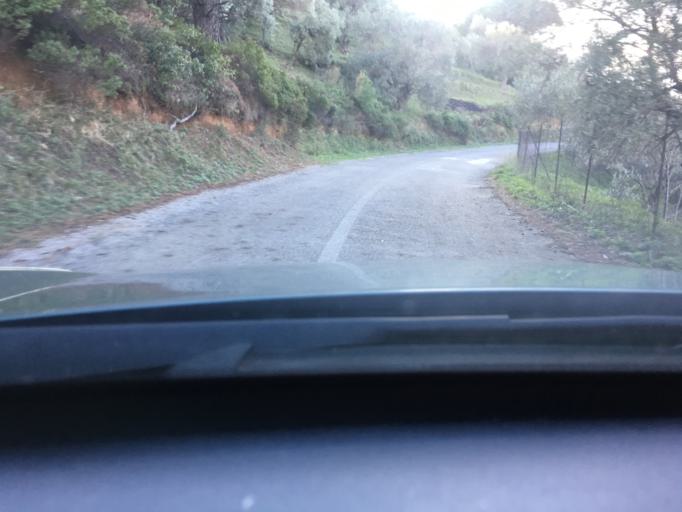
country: GR
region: Thessaly
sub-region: Nomos Magnisias
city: Skopelos
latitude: 39.1778
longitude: 23.6336
